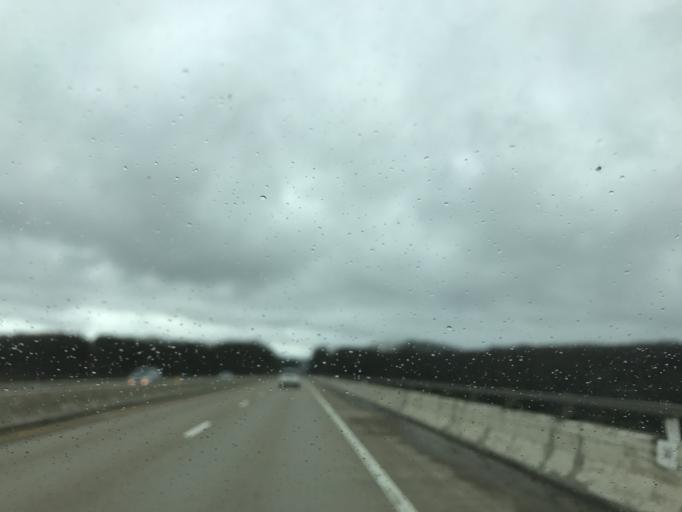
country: US
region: West Virginia
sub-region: Fayette County
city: Fayetteville
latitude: 38.0689
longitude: -81.0829
